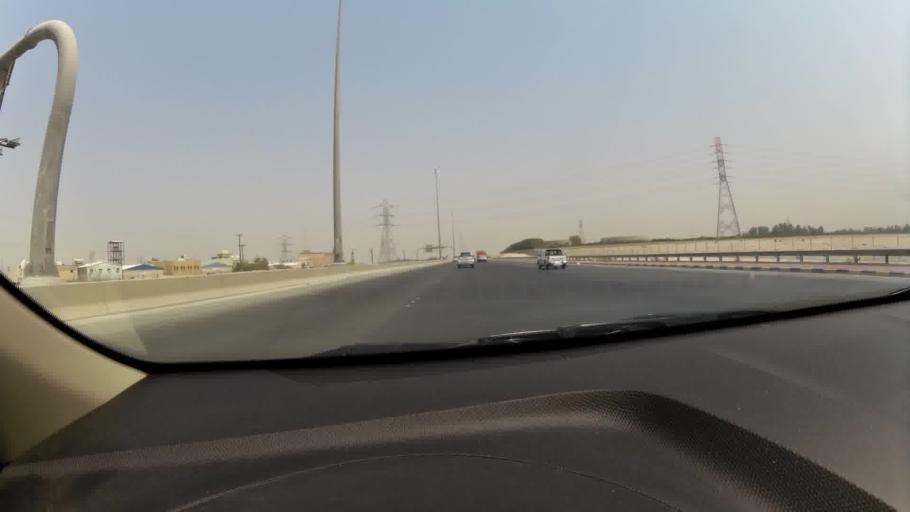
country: KW
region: Muhafazat al Jahra'
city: Al Jahra'
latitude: 29.2940
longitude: 47.7443
